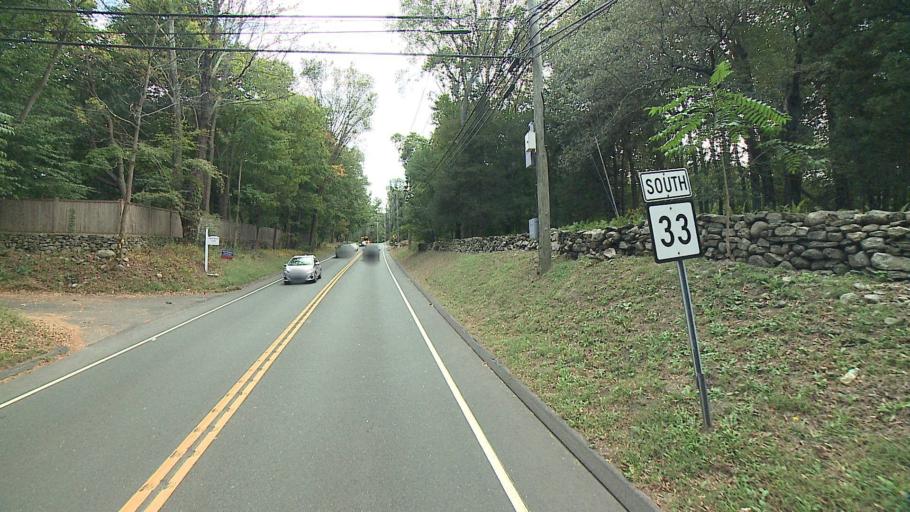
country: US
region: Connecticut
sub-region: Fairfield County
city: Westport
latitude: 41.1614
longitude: -73.3750
